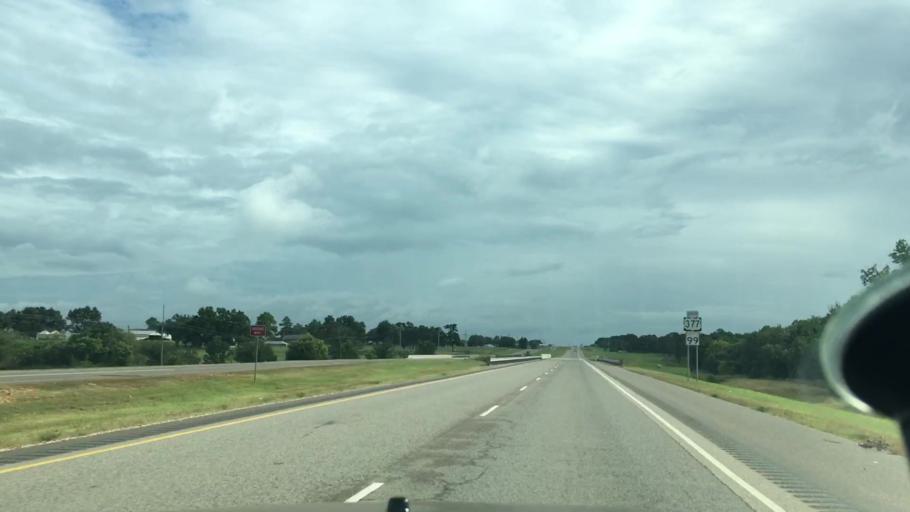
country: US
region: Oklahoma
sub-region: Lincoln County
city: Prague
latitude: 35.3624
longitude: -96.6718
